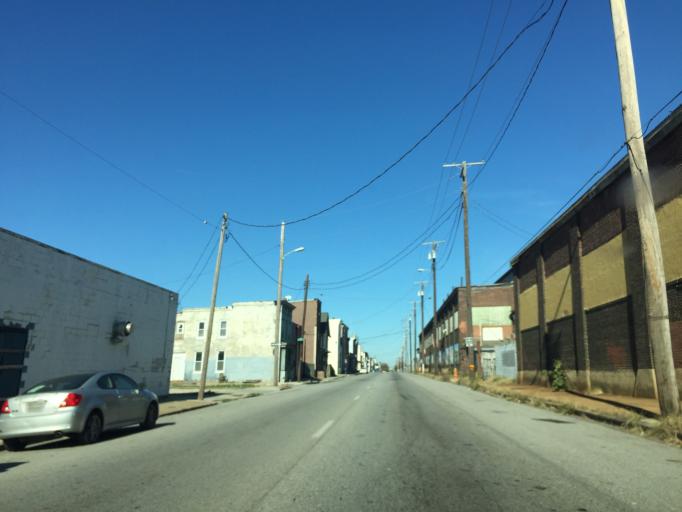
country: US
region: Maryland
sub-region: Anne Arundel County
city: Brooklyn Park
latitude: 39.2213
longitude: -76.5865
